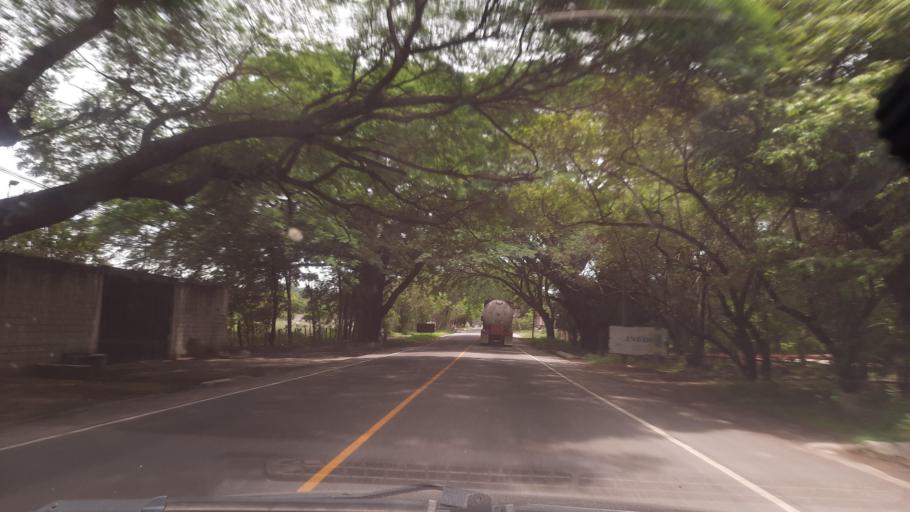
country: GT
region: Zacapa
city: Rio Hondo
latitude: 15.0862
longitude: -89.4687
